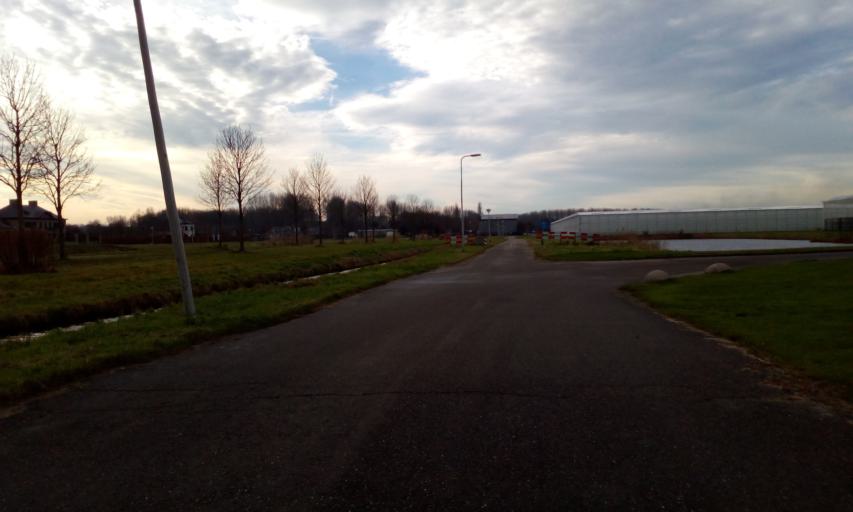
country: NL
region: South Holland
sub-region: Gemeente Lansingerland
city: Bleiswijk
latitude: 51.9799
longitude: 4.5293
